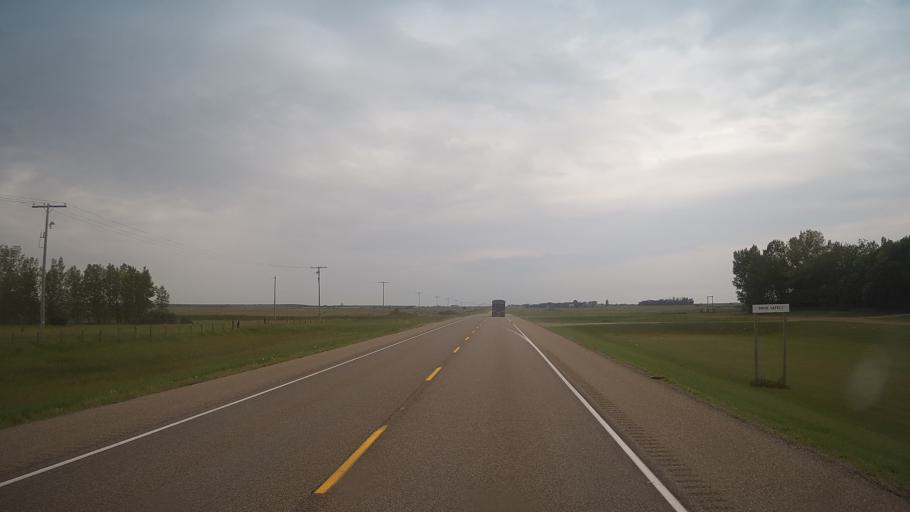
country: CA
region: Saskatchewan
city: Langham
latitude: 52.1289
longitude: -107.1433
